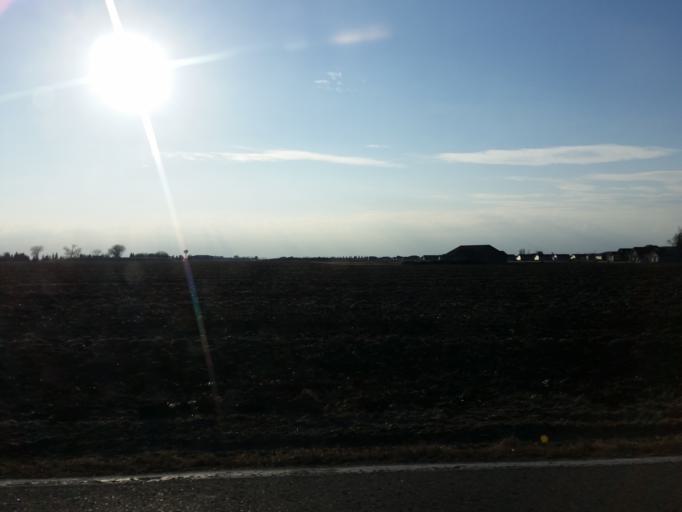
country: US
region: North Dakota
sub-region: Grand Forks County
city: Grand Forks
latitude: 47.8634
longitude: -97.0291
